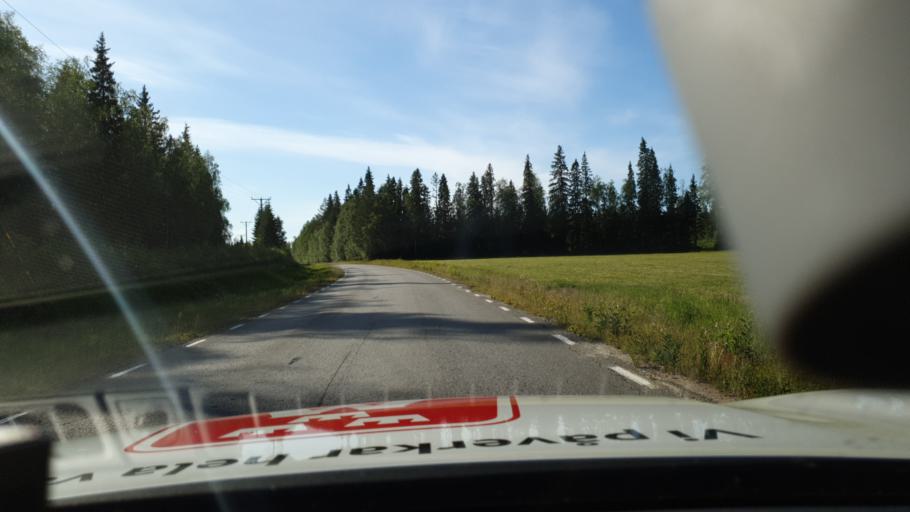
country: SE
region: Norrbotten
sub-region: Kalix Kommun
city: Toere
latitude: 65.8951
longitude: 22.6316
